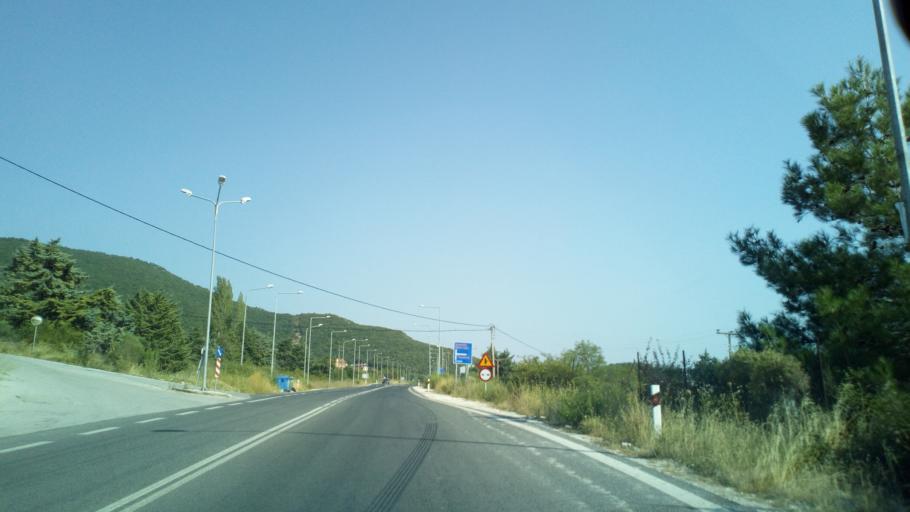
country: GR
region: Central Macedonia
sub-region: Nomos Chalkidikis
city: Polygyros
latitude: 40.3751
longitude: 23.4516
